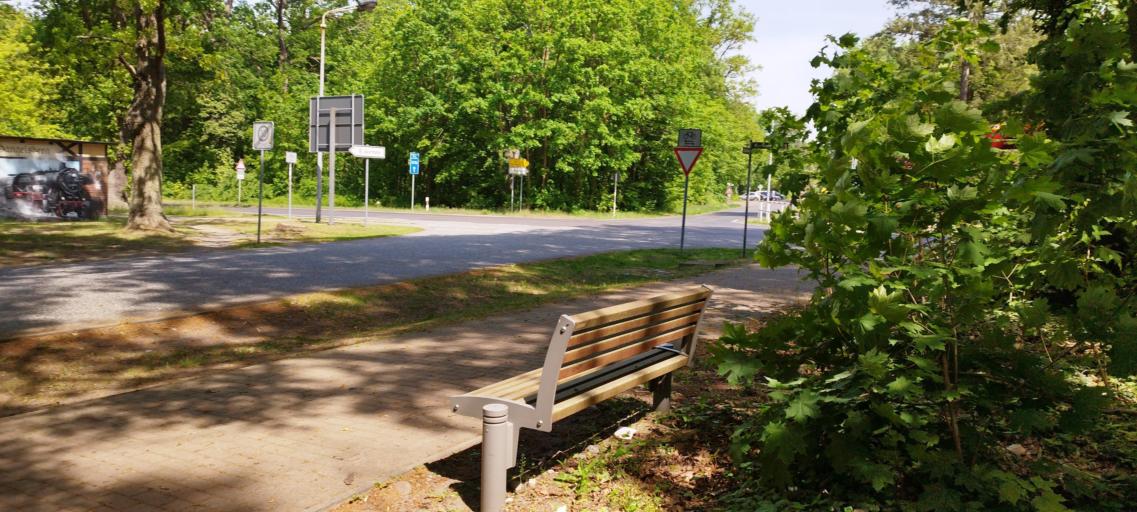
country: DE
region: Brandenburg
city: Spreenhagen
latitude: 52.3980
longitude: 13.9209
